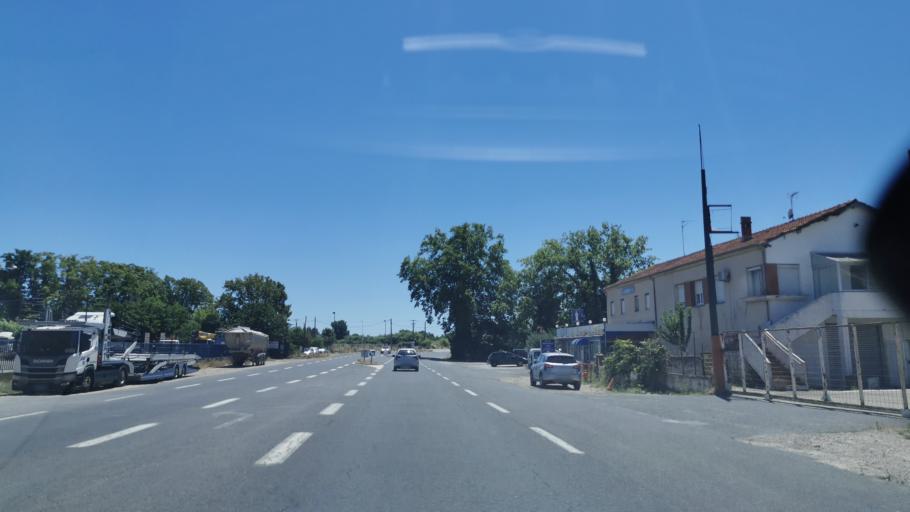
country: FR
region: Languedoc-Roussillon
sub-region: Departement de l'Herault
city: Beziers
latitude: 43.3301
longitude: 3.1938
